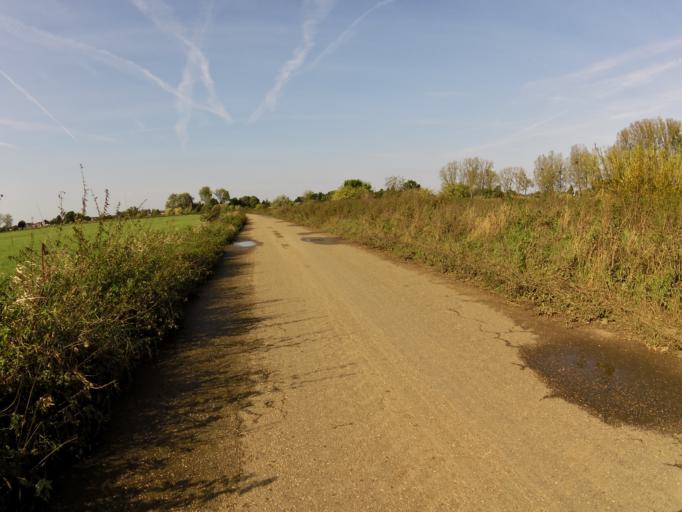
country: NL
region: Limburg
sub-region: Gemeente Stein
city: Stein
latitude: 50.9593
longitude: 5.7511
